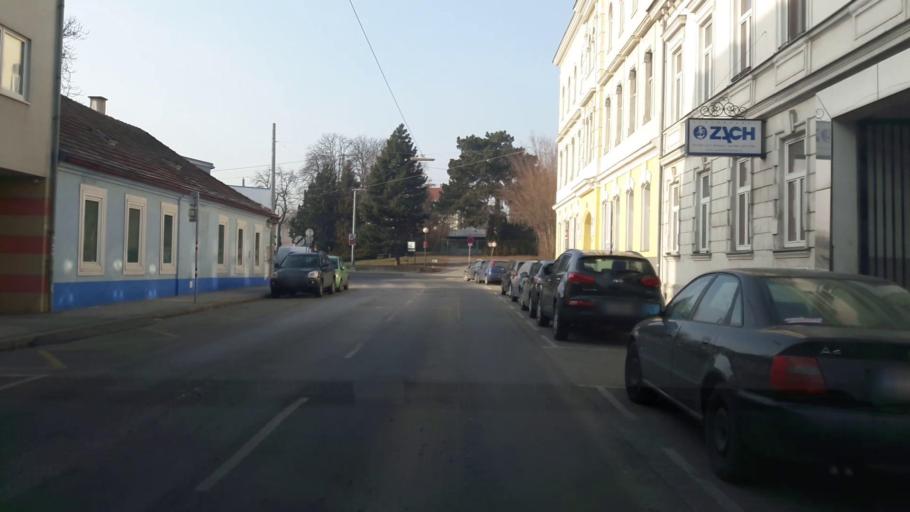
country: AT
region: Lower Austria
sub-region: Politischer Bezirk Modling
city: Perchtoldsdorf
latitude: 48.1480
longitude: 16.2910
